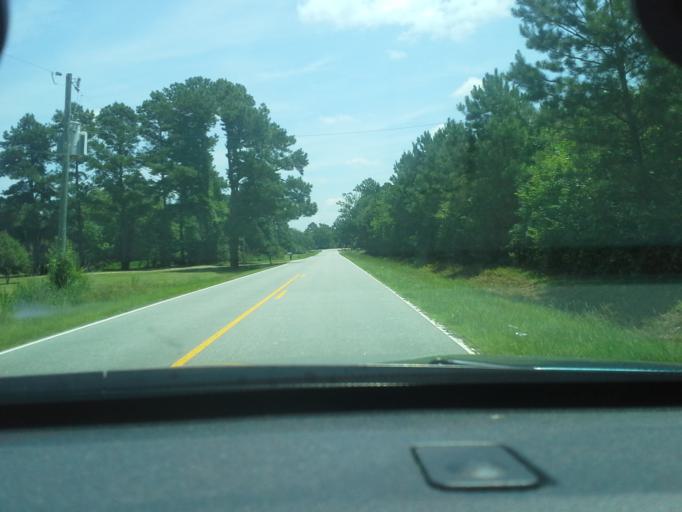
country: US
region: North Carolina
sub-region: Chowan County
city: Edenton
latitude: 35.9252
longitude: -76.5949
